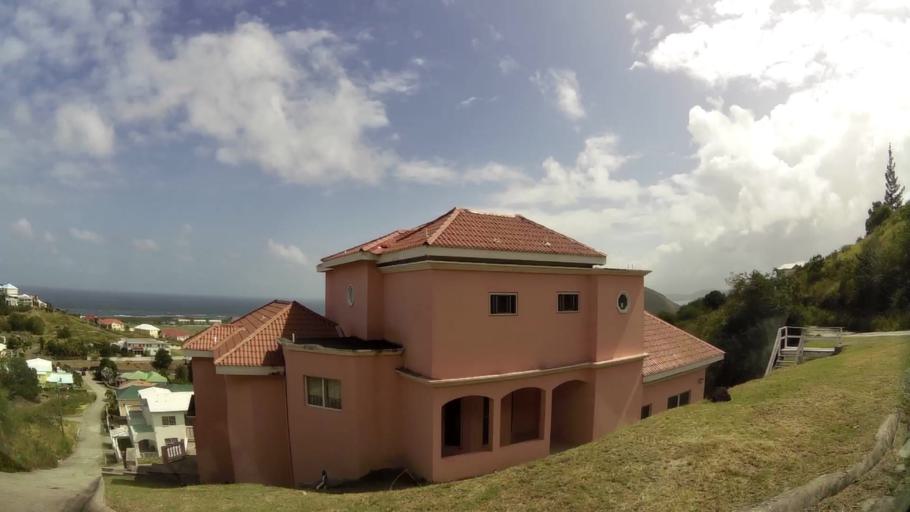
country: KN
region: Saint George Basseterre
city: Basseterre
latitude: 17.2929
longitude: -62.6975
